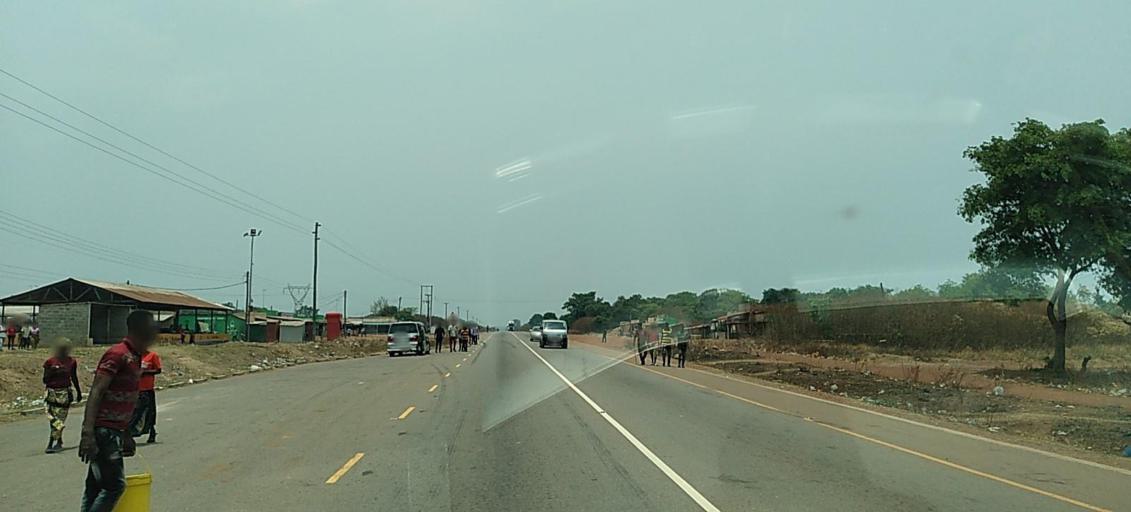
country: ZM
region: Copperbelt
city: Chililabombwe
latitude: -12.3910
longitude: 27.3589
